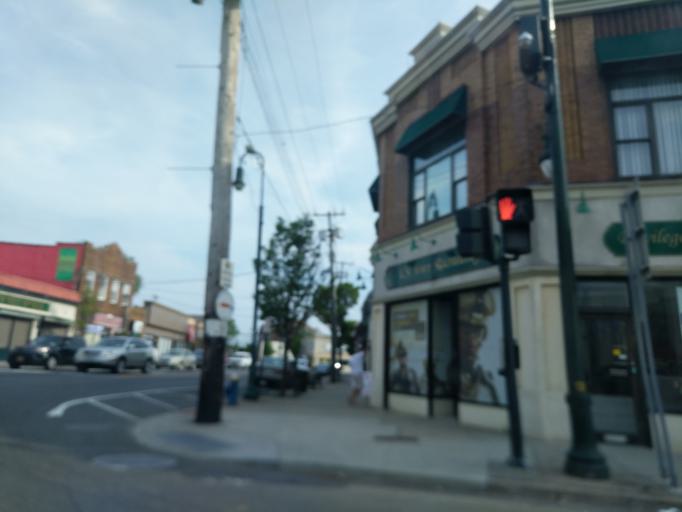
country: US
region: New York
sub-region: Nassau County
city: Lynbrook
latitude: 40.6548
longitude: -73.6719
